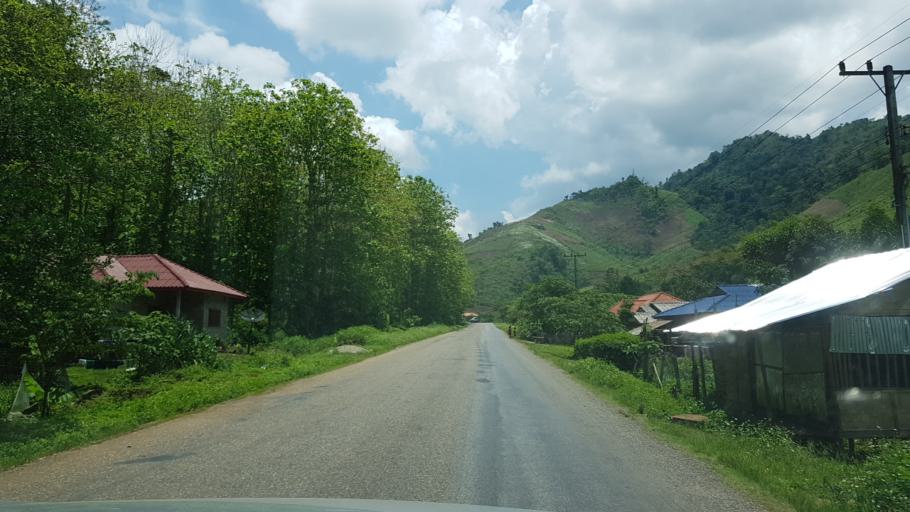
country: LA
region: Vientiane
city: Muang Kasi
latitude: 19.1325
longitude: 102.2816
